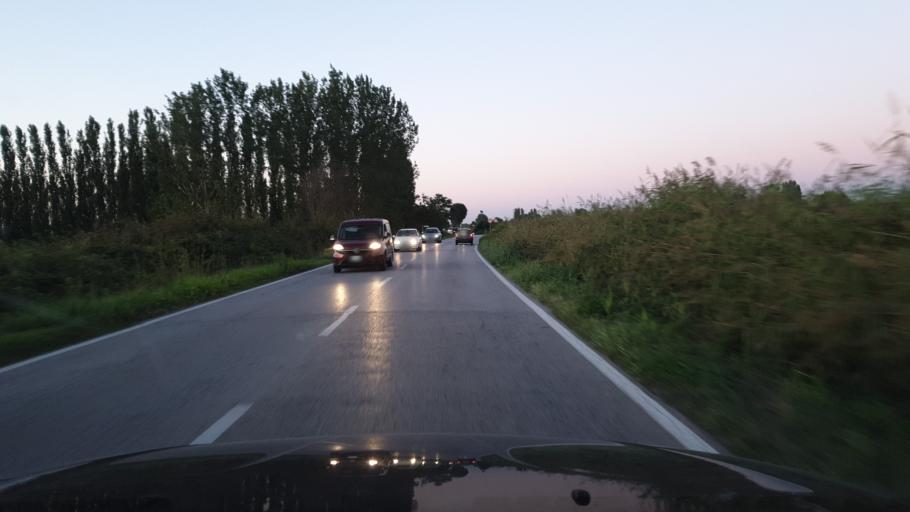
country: IT
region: Emilia-Romagna
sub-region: Provincia di Bologna
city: Altedo
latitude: 44.6532
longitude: 11.4852
